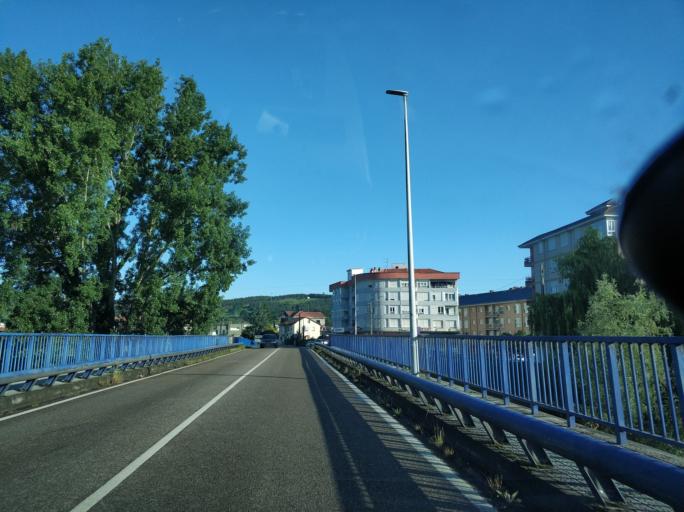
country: ES
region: Cantabria
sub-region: Provincia de Cantabria
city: Puente Viesgo
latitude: 43.3563
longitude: -3.9623
